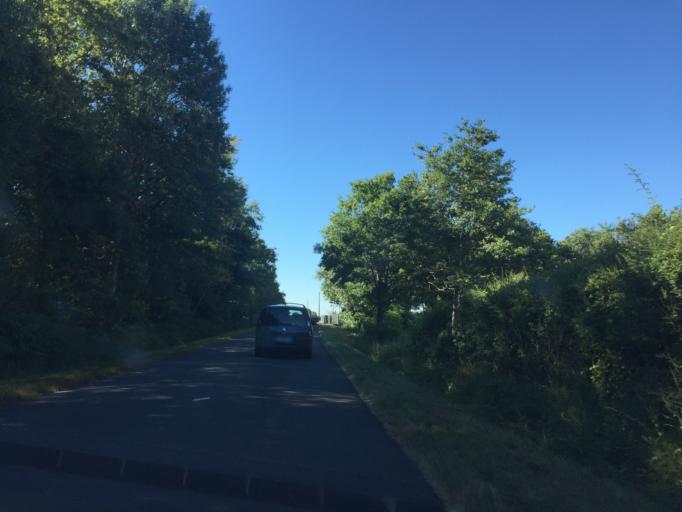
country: FR
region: Auvergne
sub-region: Departement de l'Allier
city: Dompierre-sur-Besbre
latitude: 46.5270
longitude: 3.6199
